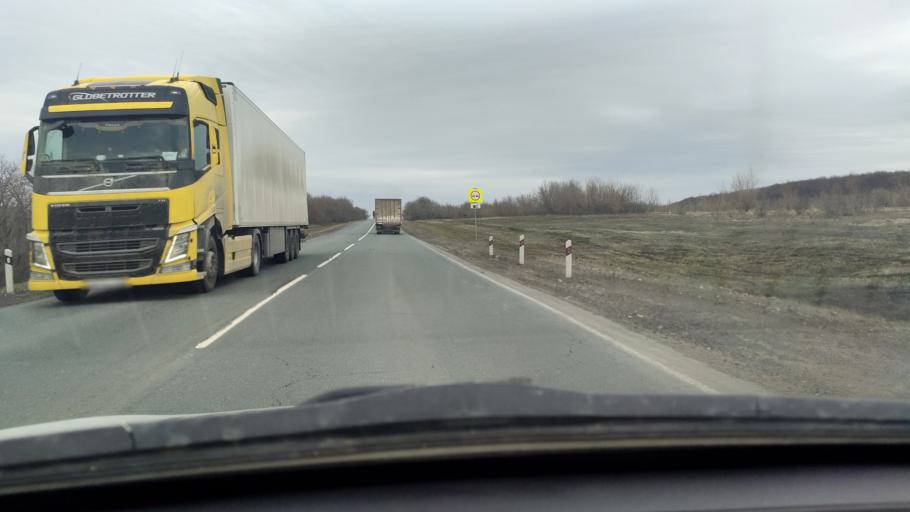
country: RU
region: Samara
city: Zhigulevsk
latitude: 53.3044
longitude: 49.3488
